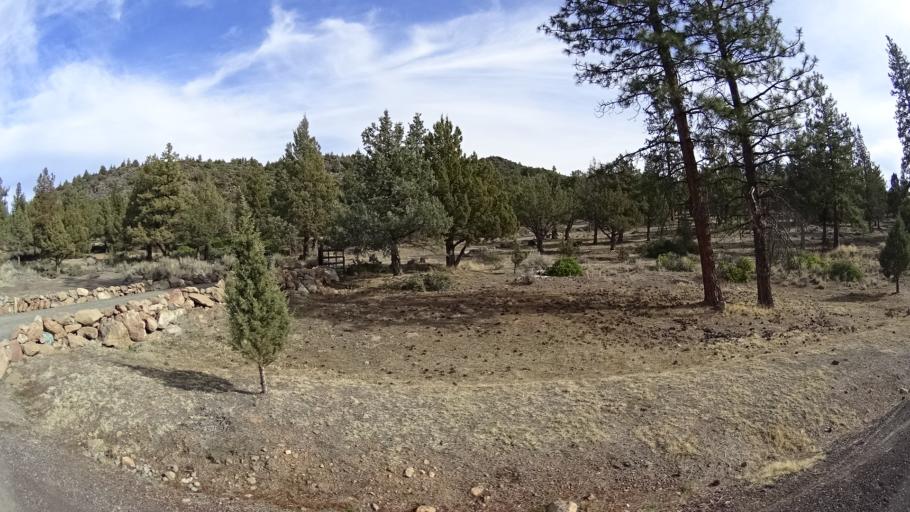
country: US
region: California
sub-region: Siskiyou County
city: Weed
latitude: 41.5172
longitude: -122.3666
